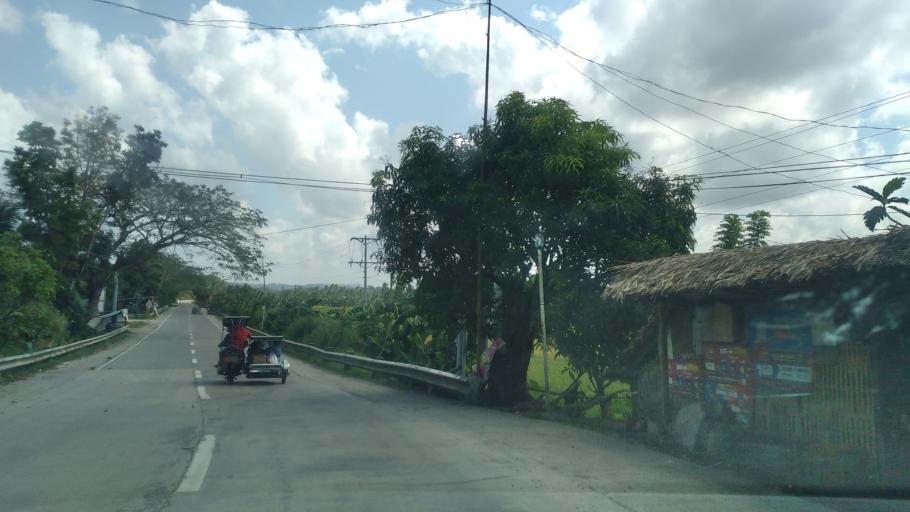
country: PH
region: Calabarzon
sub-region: Province of Quezon
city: Macalelon
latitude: 13.7555
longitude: 122.1445
